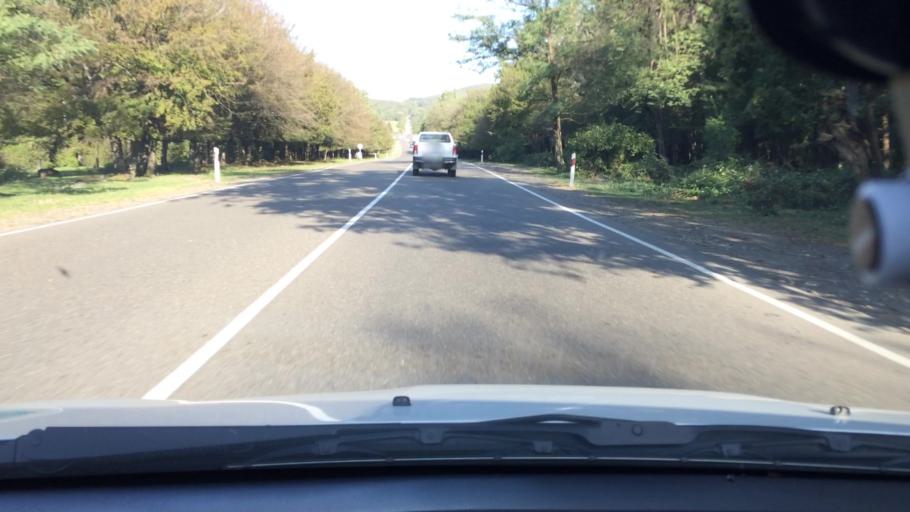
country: GE
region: Imereti
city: Kutaisi
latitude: 42.2346
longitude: 42.7727
